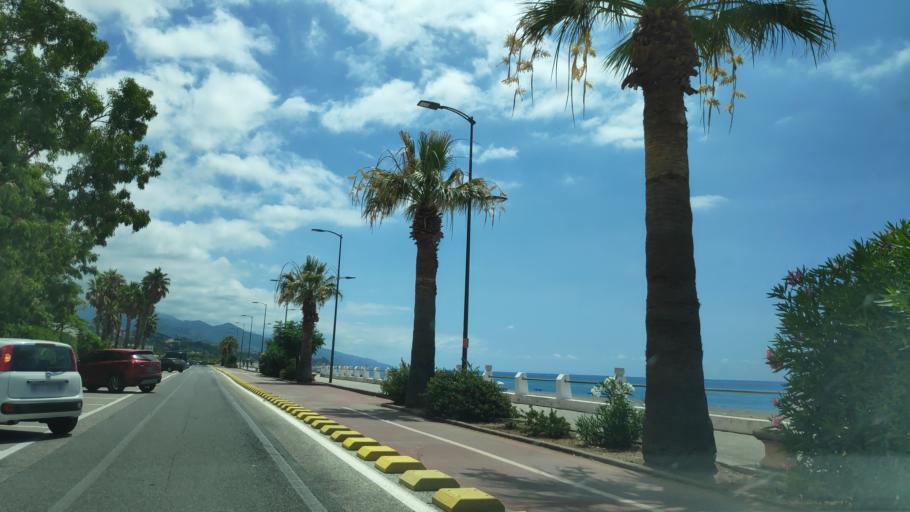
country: IT
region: Calabria
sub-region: Provincia di Cosenza
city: Paola
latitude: 39.3563
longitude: 16.0329
